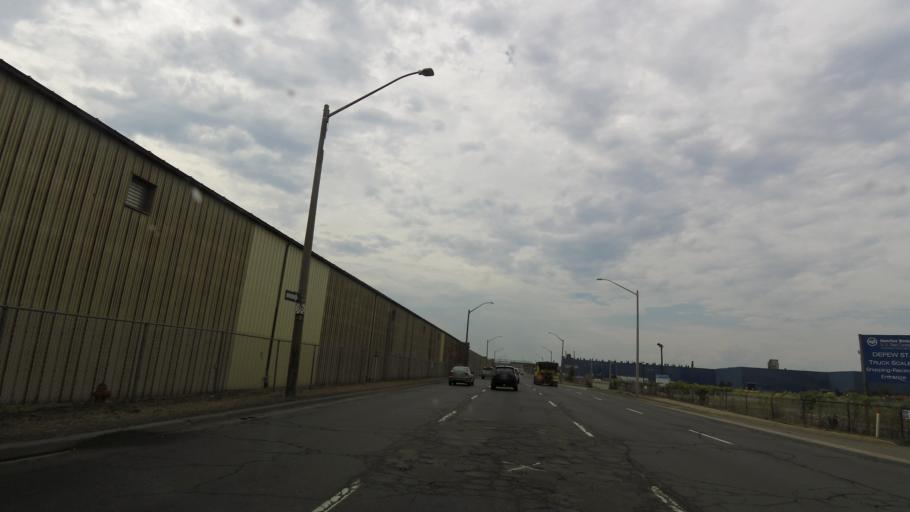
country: CA
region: Ontario
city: Hamilton
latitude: 43.2628
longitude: -79.8133
